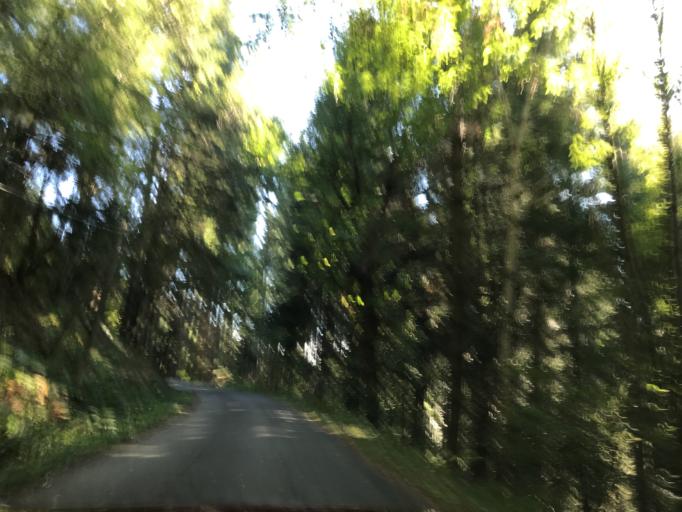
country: FR
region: Auvergne
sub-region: Departement du Puy-de-Dome
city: Escoutoux
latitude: 45.7833
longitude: 3.6077
